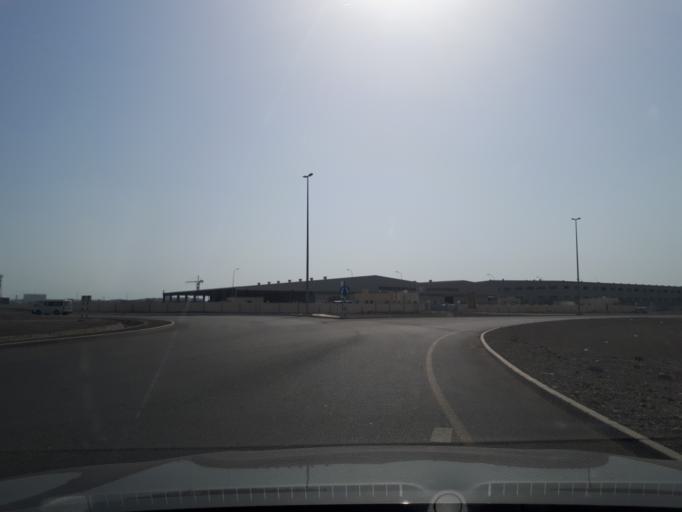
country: OM
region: Al Batinah
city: Al Liwa'
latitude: 24.4360
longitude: 56.5788
